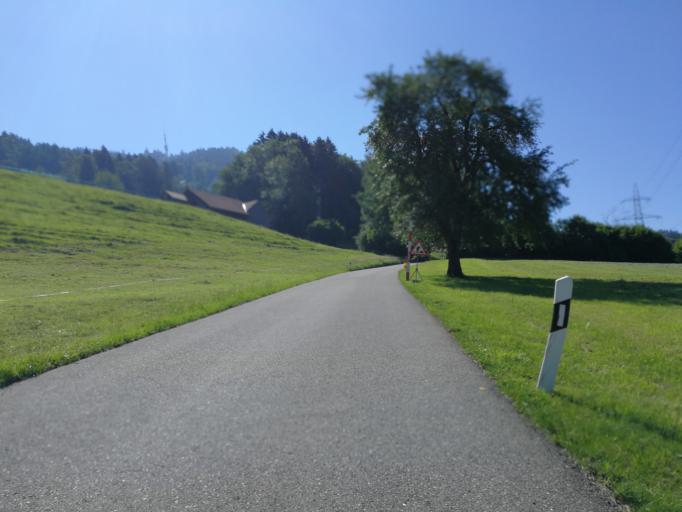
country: CH
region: Zurich
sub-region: Bezirk Hinwil
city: Hadlikon
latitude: 47.2978
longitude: 8.8723
